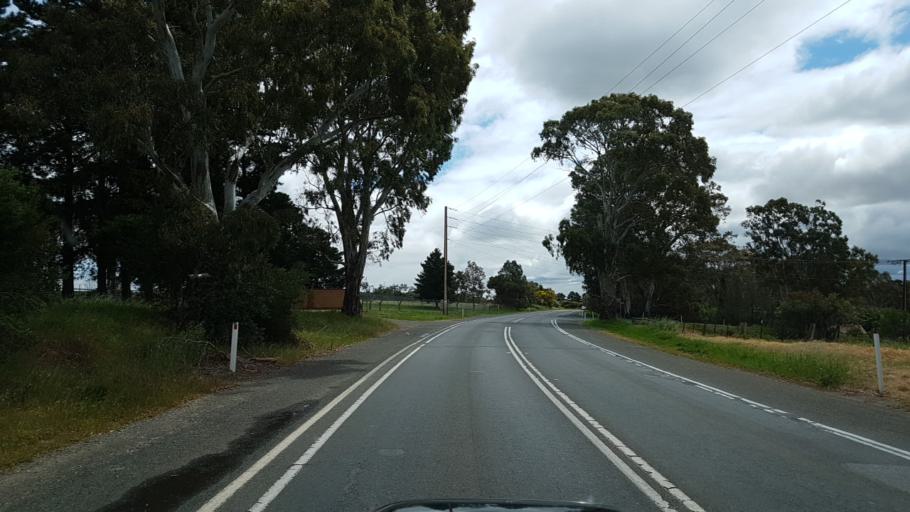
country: AU
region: South Australia
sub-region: Playford
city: One Tree Hill
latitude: -34.7176
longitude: 138.7564
